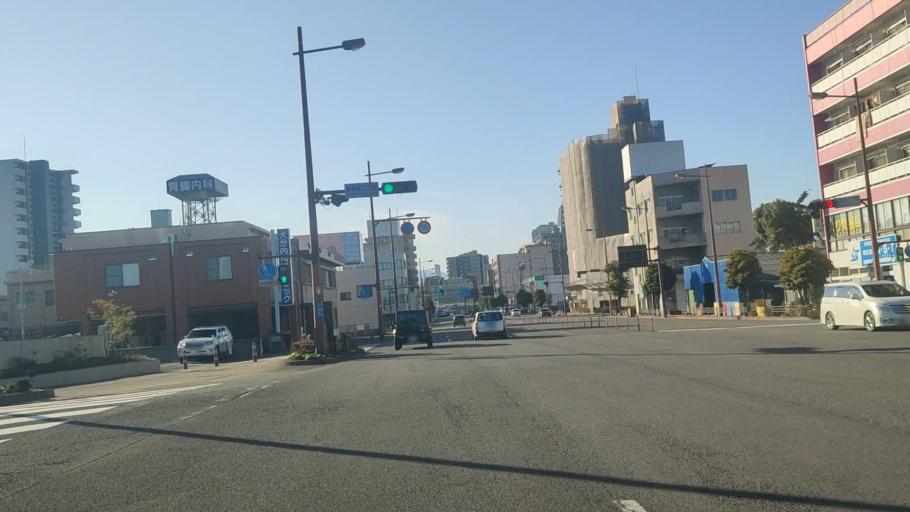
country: JP
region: Oita
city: Oita
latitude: 33.2317
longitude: 131.6170
